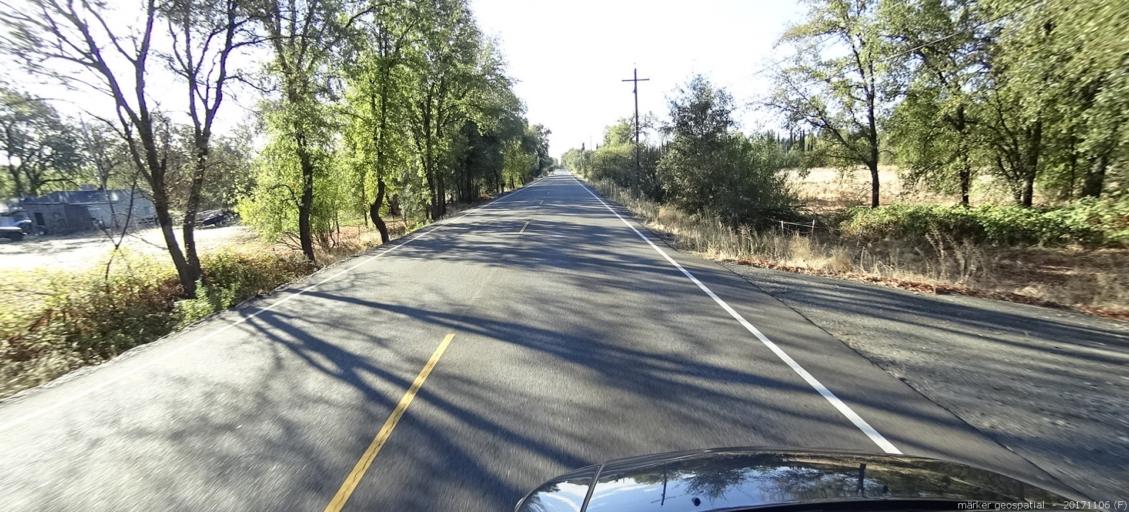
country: US
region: California
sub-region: Shasta County
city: Bella Vista
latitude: 40.6076
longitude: -122.2347
